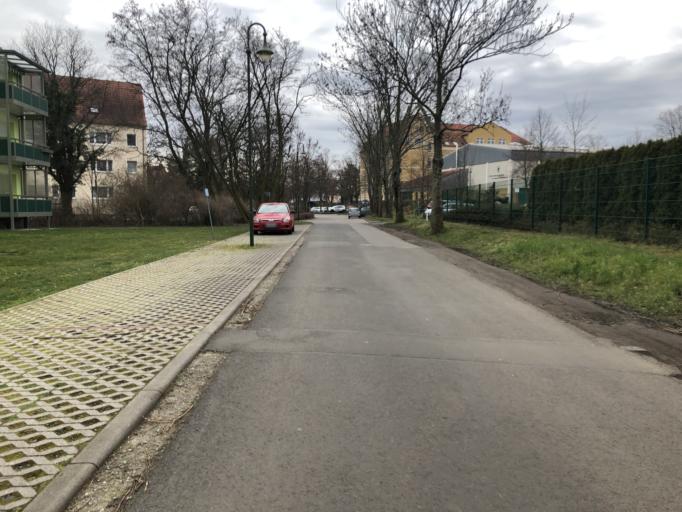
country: DE
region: Saxony
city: Grossposna
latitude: 51.2859
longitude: 12.4612
